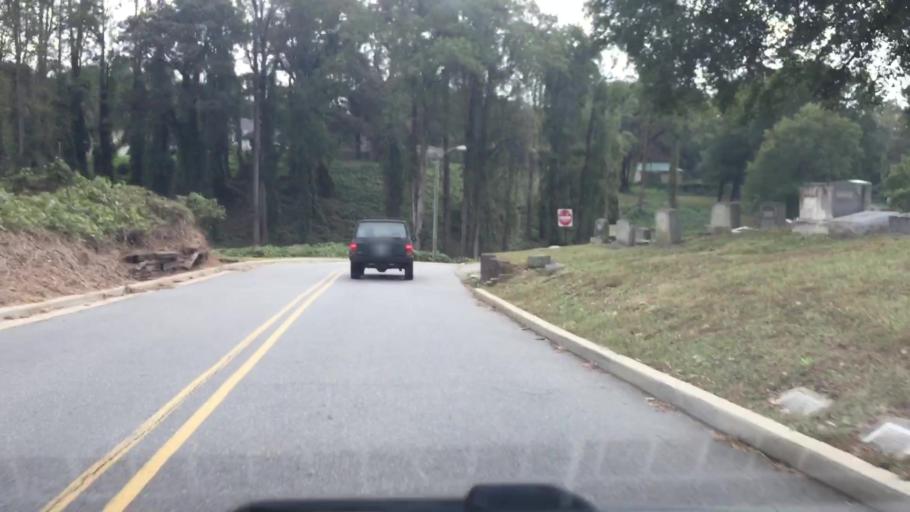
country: US
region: North Carolina
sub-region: Iredell County
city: Mooresville
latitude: 35.5796
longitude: -80.8113
